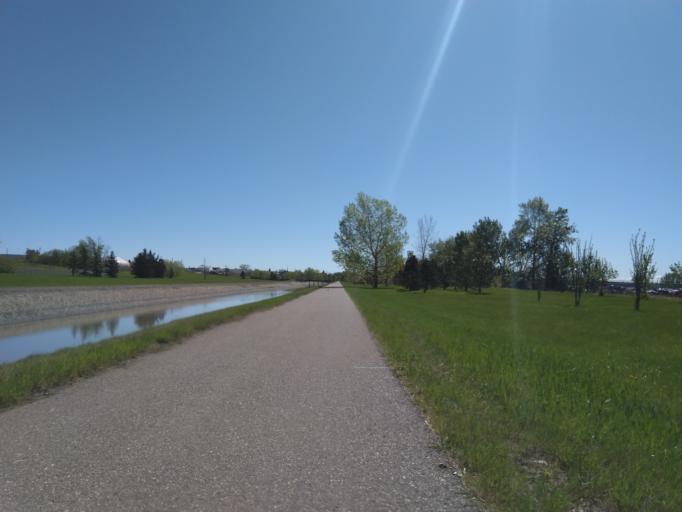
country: CA
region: Alberta
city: Calgary
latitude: 51.0022
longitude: -114.0090
